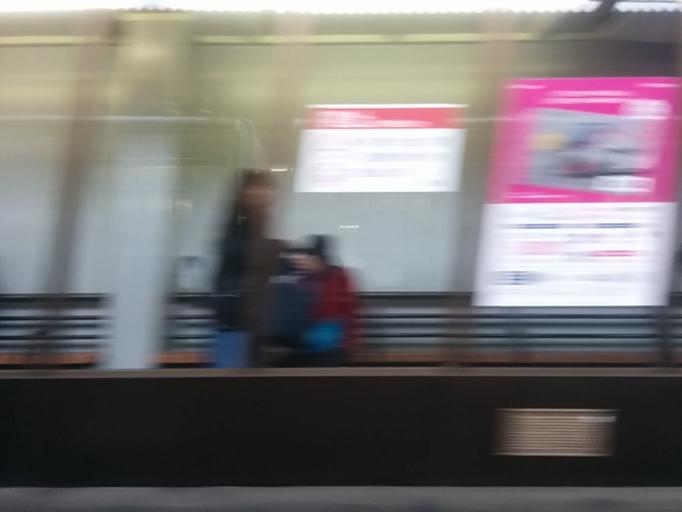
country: JP
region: Tokyo
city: Kokubunji
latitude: 35.6683
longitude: 139.4684
